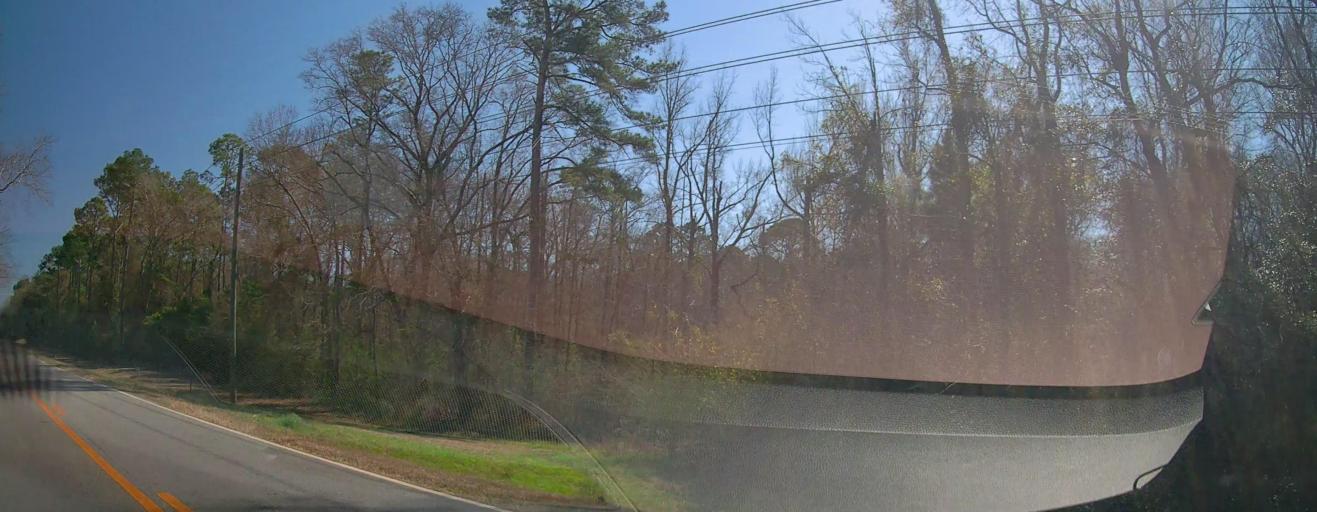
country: US
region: Georgia
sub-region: Houston County
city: Perry
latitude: 32.4942
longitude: -83.6603
